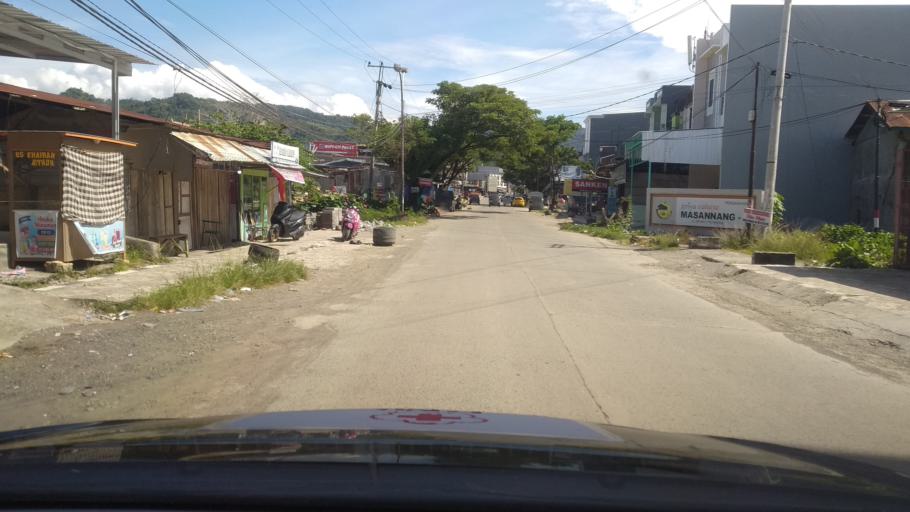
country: ID
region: Sulawesi Barat
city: Mamuju
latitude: -2.6856
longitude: 118.8766
